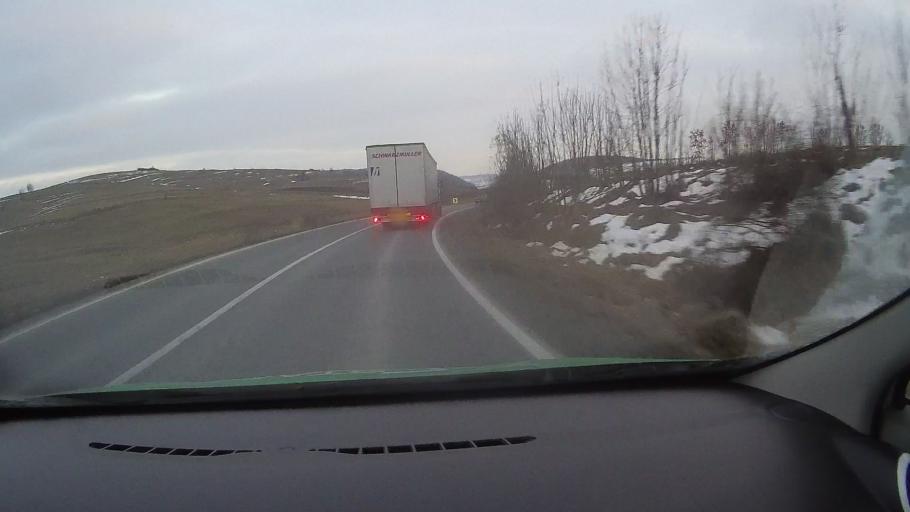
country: RO
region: Harghita
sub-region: Comuna Lupeni
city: Lupeni
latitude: 46.3502
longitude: 25.2628
